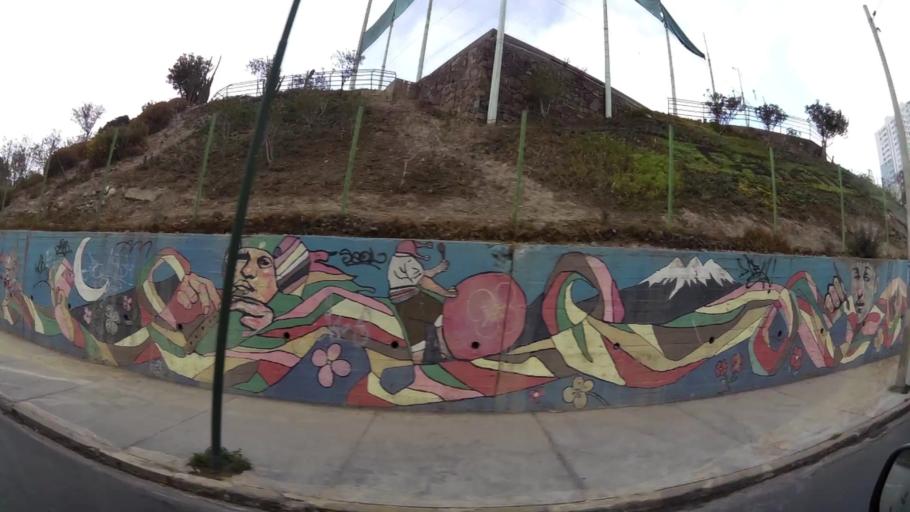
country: BO
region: La Paz
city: La Paz
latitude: -16.5035
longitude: -68.1267
